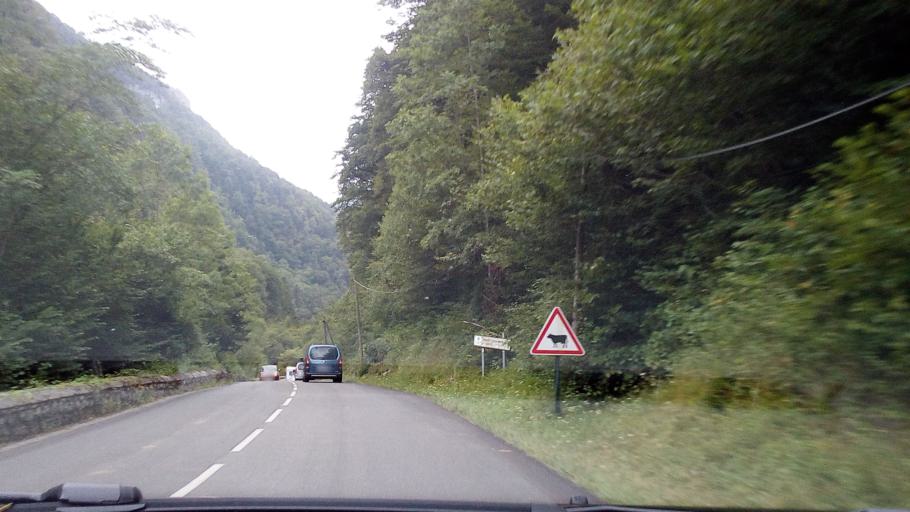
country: FR
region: Aquitaine
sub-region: Departement des Pyrenees-Atlantiques
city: Laruns
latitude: 42.9437
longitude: -0.4430
